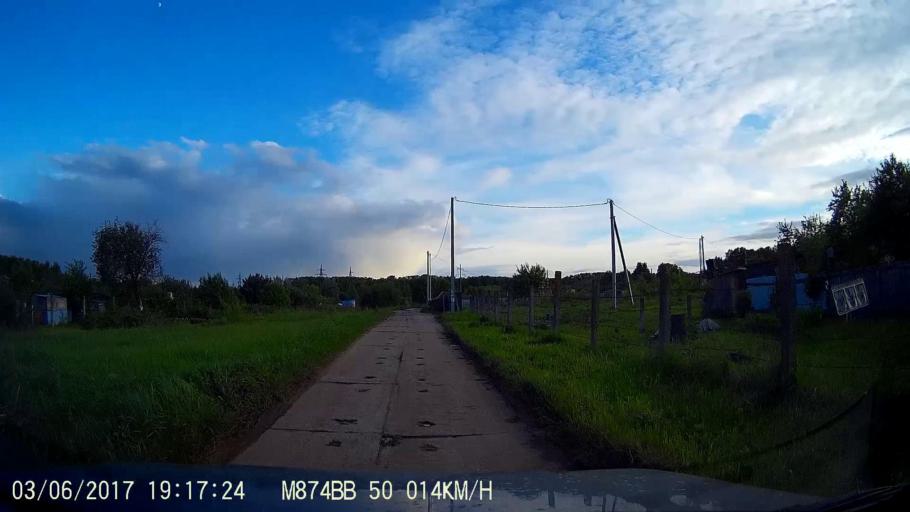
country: RU
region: Moskovskaya
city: Sychevo
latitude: 55.0700
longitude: 38.7369
